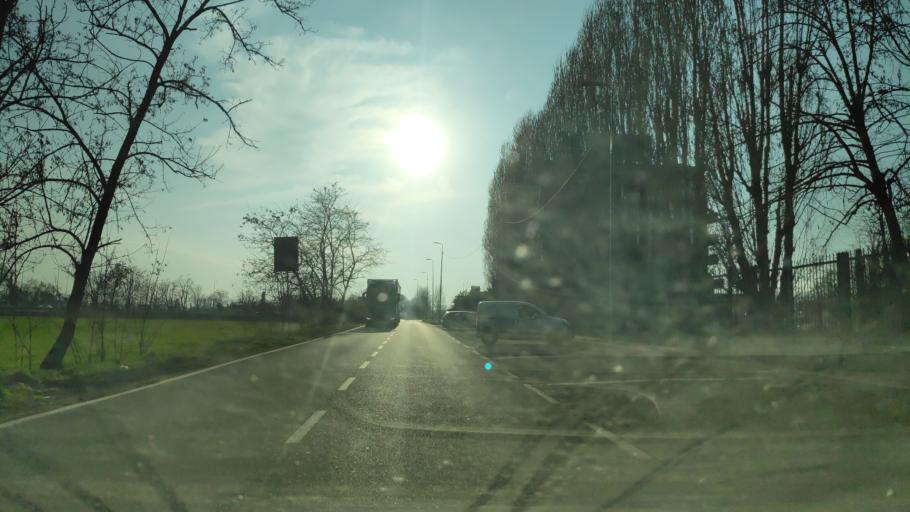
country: IT
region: Lombardy
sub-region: Citta metropolitana di Milano
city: Settimo Milanese
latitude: 45.4583
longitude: 9.0719
